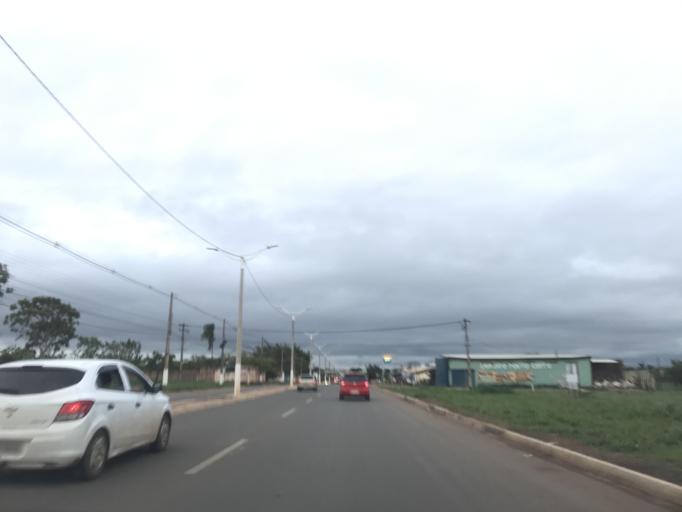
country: BR
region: Goias
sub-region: Luziania
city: Luziania
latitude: -16.2258
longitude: -47.9374
